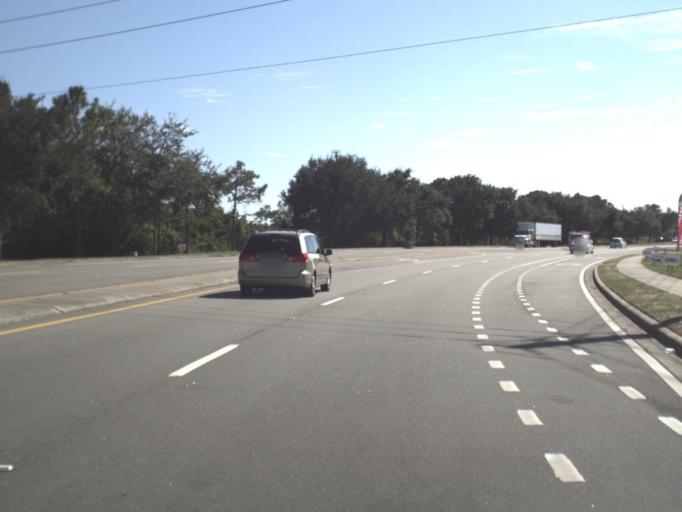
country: US
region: Florida
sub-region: Brevard County
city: South Patrick Shores
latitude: 28.2143
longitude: -80.6725
